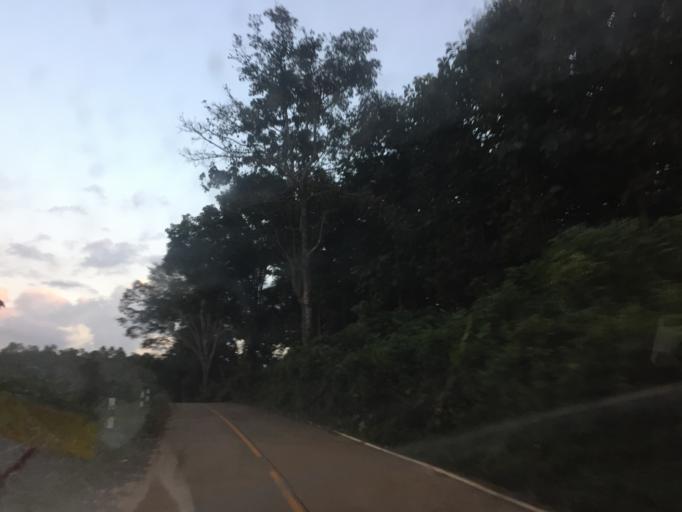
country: TH
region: Chiang Mai
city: Samoeng
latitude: 18.9992
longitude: 98.7153
